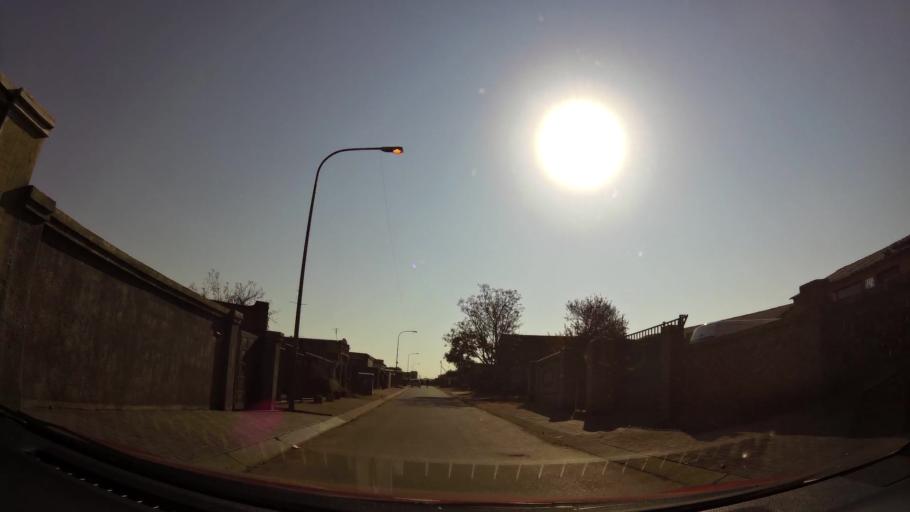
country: ZA
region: Gauteng
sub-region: City of Johannesburg Metropolitan Municipality
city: Soweto
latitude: -26.2488
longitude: 27.9525
